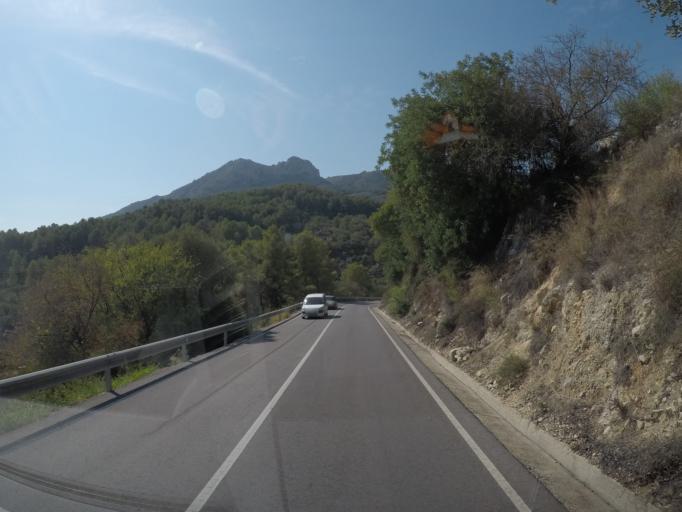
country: ES
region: Valencia
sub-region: Provincia de Alicante
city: Murla
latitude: 38.7809
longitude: -0.0980
